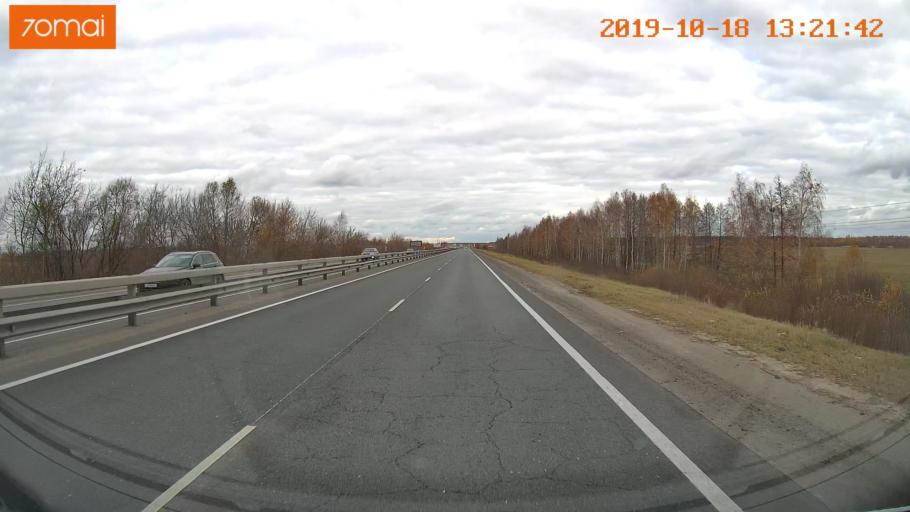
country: RU
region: Rjazan
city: Polyany
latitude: 54.6985
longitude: 39.8411
